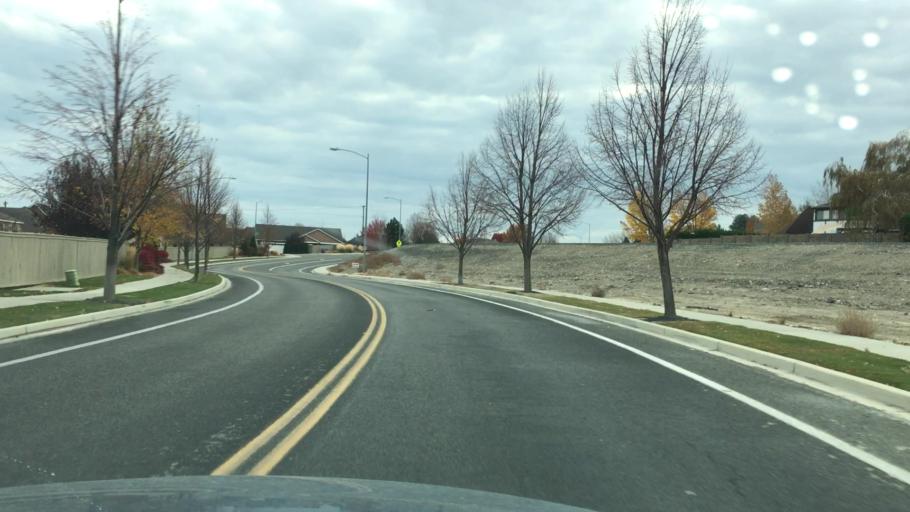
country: US
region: Washington
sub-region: Franklin County
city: West Pasco
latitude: 46.1880
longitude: -119.1937
